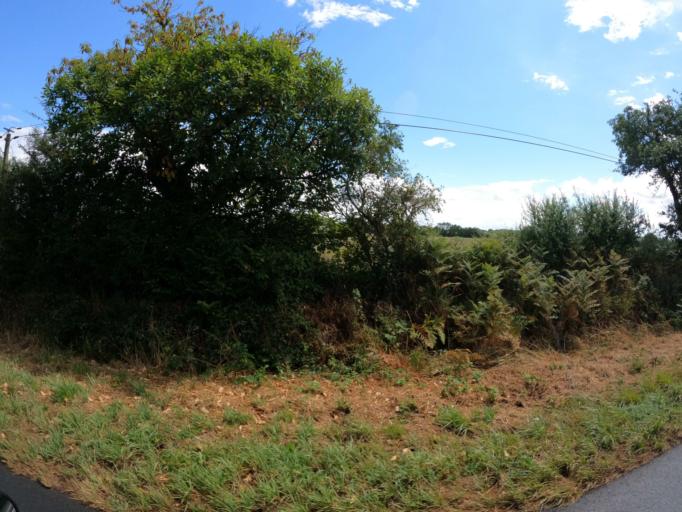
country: FR
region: Pays de la Loire
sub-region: Departement de Maine-et-Loire
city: Feneu
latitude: 47.6025
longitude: -0.5872
